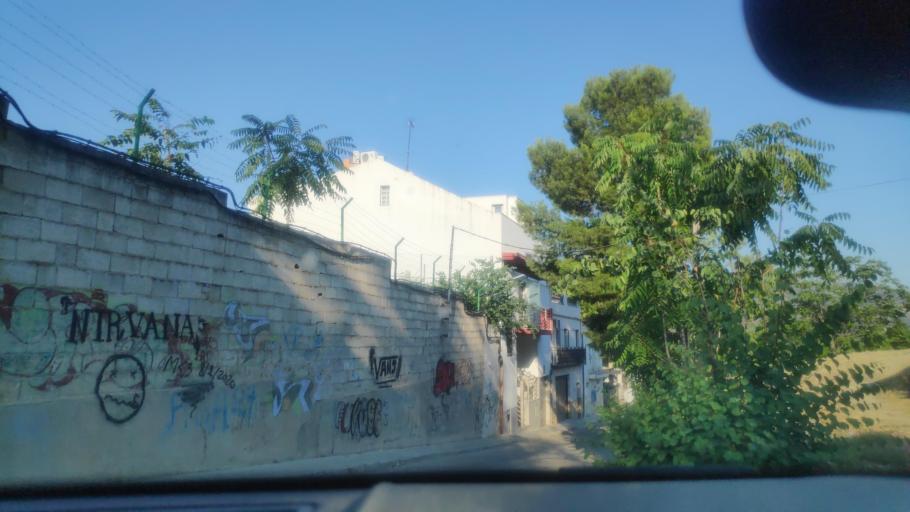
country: ES
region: Andalusia
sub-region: Provincia de Jaen
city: Jaen
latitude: 37.7677
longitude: -3.7803
